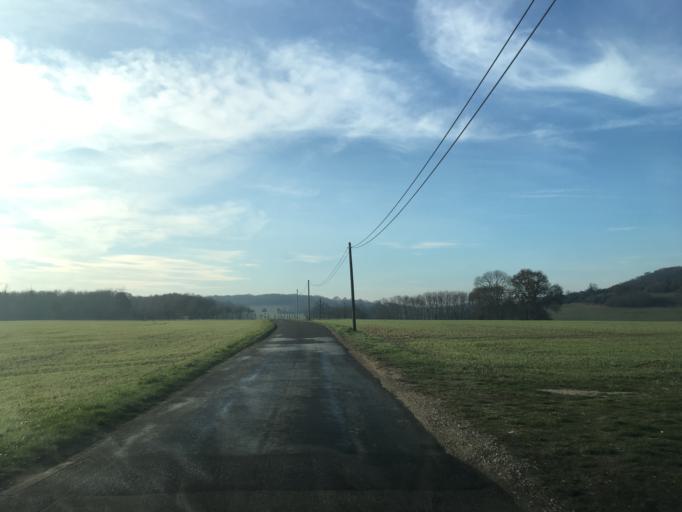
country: FR
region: Haute-Normandie
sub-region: Departement de l'Eure
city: Menilles
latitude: 49.0478
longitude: 1.2965
